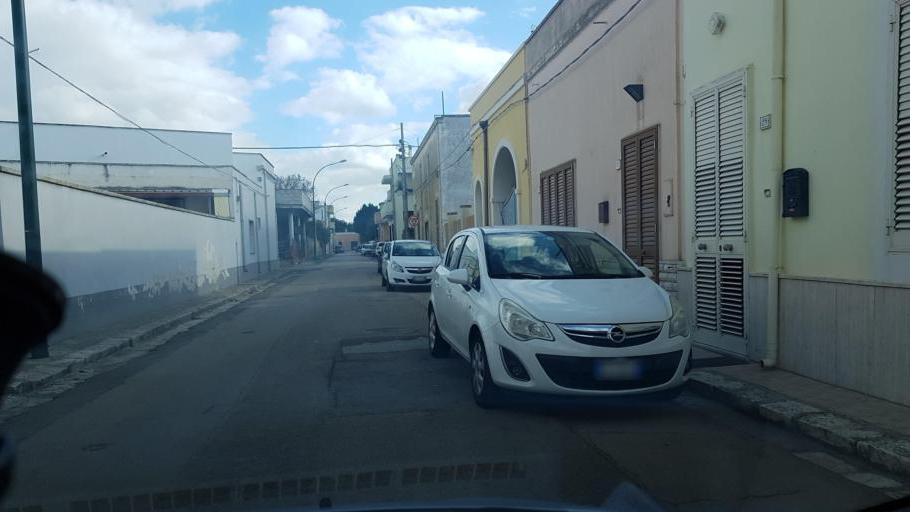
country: IT
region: Apulia
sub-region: Provincia di Lecce
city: Squinzano
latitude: 40.4418
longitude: 18.0383
